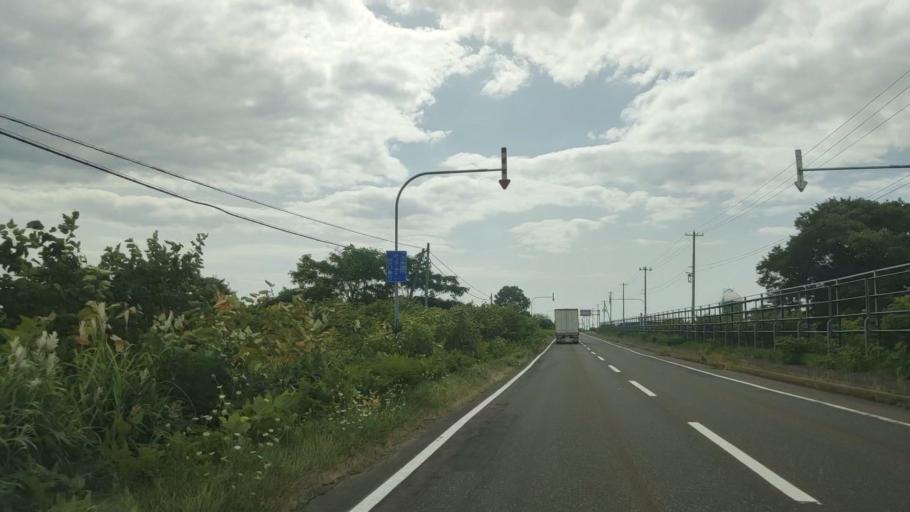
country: JP
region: Hokkaido
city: Rumoi
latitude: 44.5554
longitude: 141.7806
